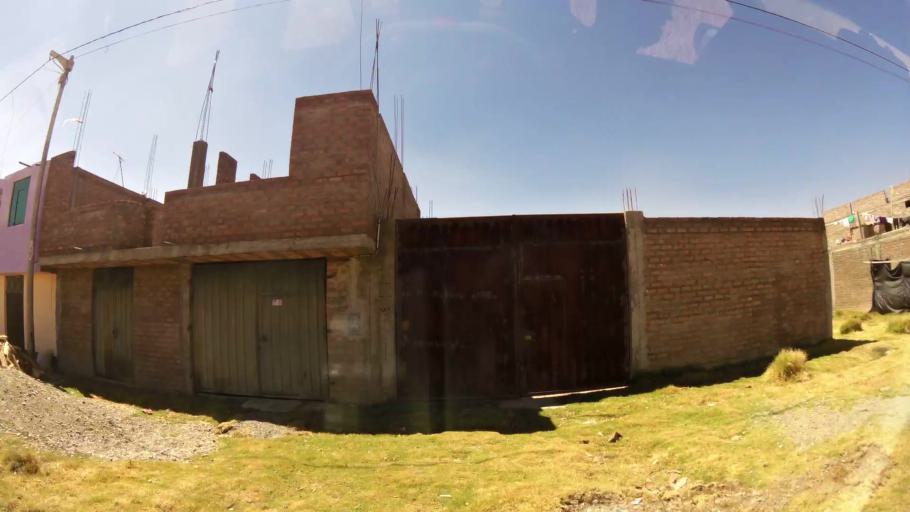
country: PE
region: Junin
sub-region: Provincia de Jauja
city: Jauja
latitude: -11.7729
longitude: -75.4909
